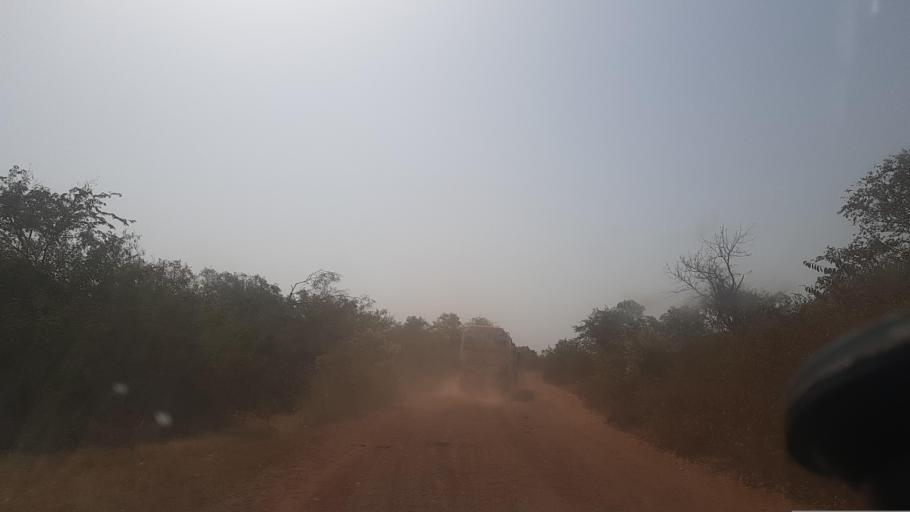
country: ML
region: Segou
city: Baroueli
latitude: 13.0728
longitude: -6.4805
